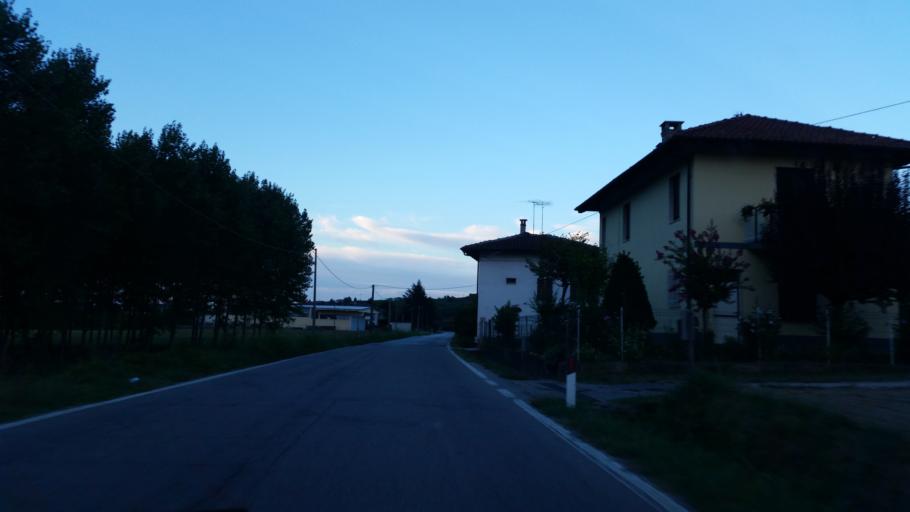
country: IT
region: Piedmont
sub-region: Provincia di Cuneo
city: Neive-Borgonovo
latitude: 44.7114
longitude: 8.1118
